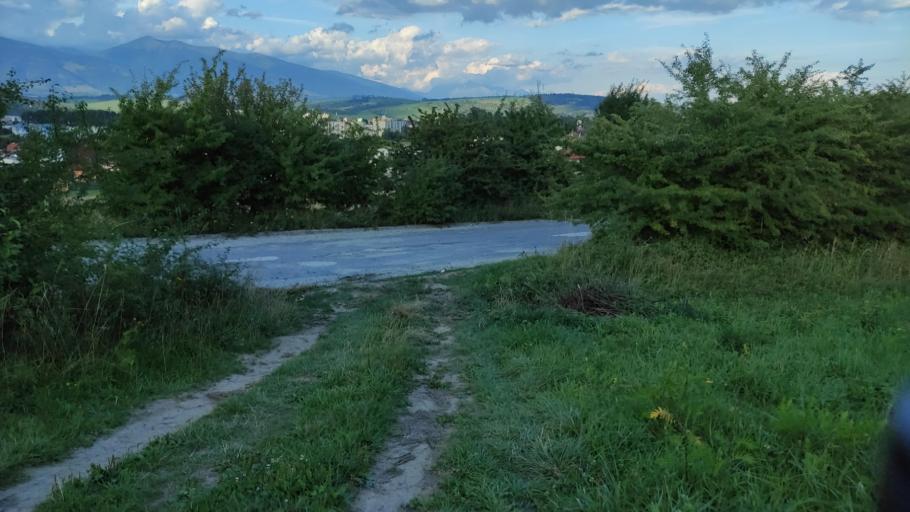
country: SK
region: Zilinsky
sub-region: Okres Liptovsky Mikulas
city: Liptovsky Mikulas
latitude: 49.0825
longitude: 19.5816
